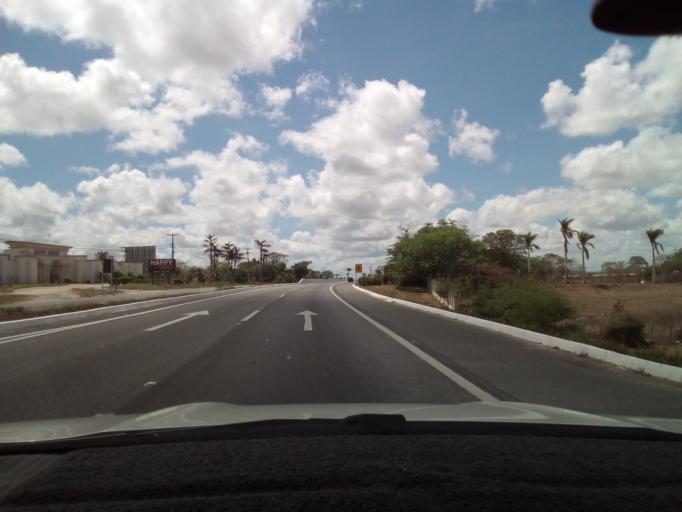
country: BR
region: Paraiba
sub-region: Campina Grande
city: Campina Grande
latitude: -7.2480
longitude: -35.8465
